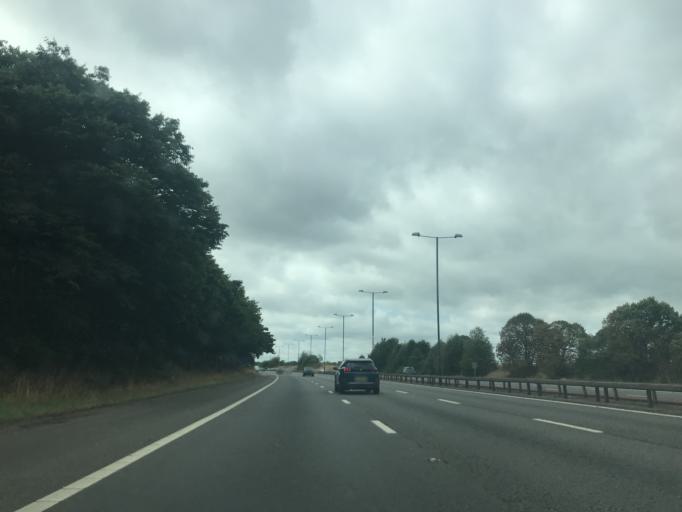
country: GB
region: England
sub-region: Greater London
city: Isleworth
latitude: 51.4950
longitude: -0.3487
